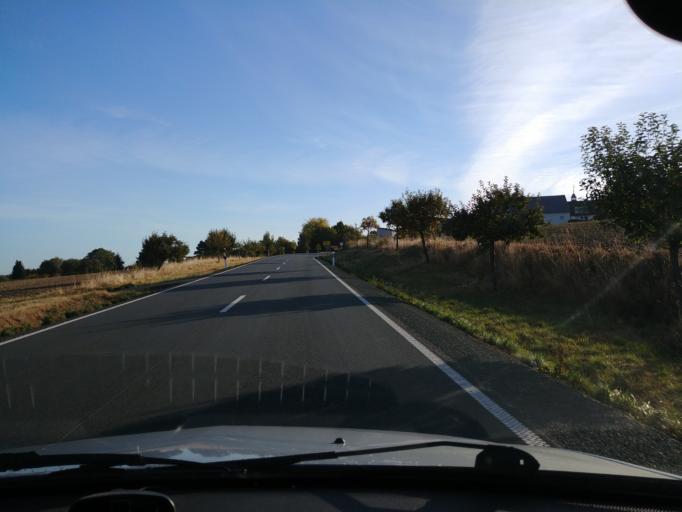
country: DE
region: Hesse
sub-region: Regierungsbezirk Darmstadt
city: Neu-Anspach
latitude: 50.3181
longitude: 8.4601
